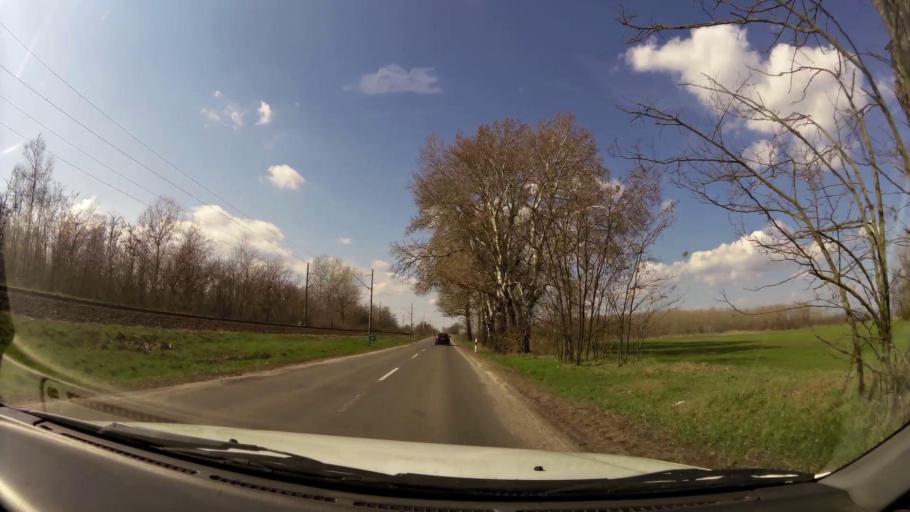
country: HU
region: Pest
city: Farmos
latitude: 47.3760
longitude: 19.7938
